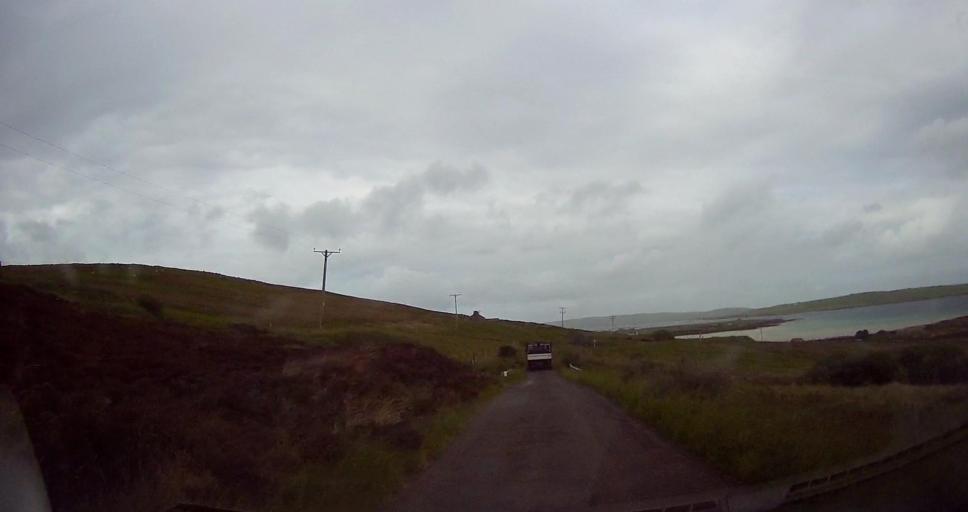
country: GB
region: Scotland
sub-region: Orkney Islands
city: Stromness
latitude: 58.9032
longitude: -3.3165
